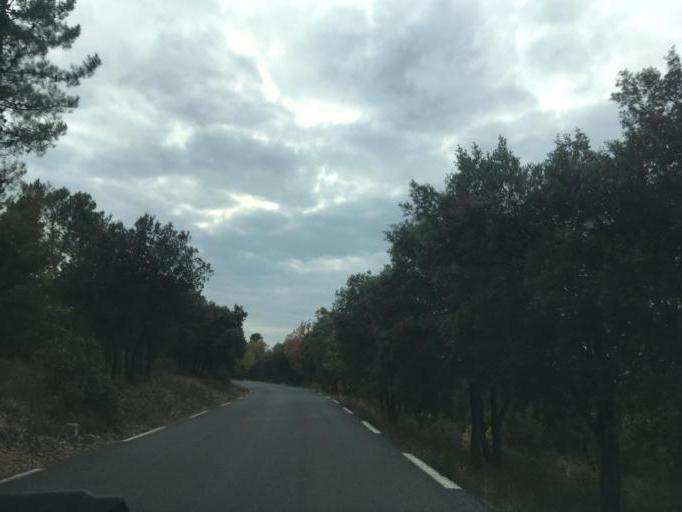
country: FR
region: Provence-Alpes-Cote d'Azur
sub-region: Departement du Var
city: Villecroze
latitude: 43.5600
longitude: 6.3309
